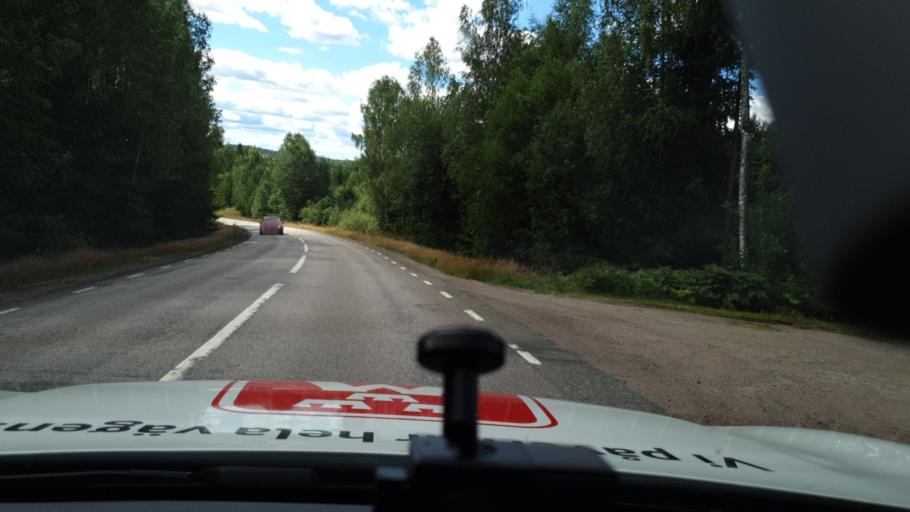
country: SE
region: Vaermland
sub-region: Sunne Kommun
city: Sunne
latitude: 59.6797
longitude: 13.0407
